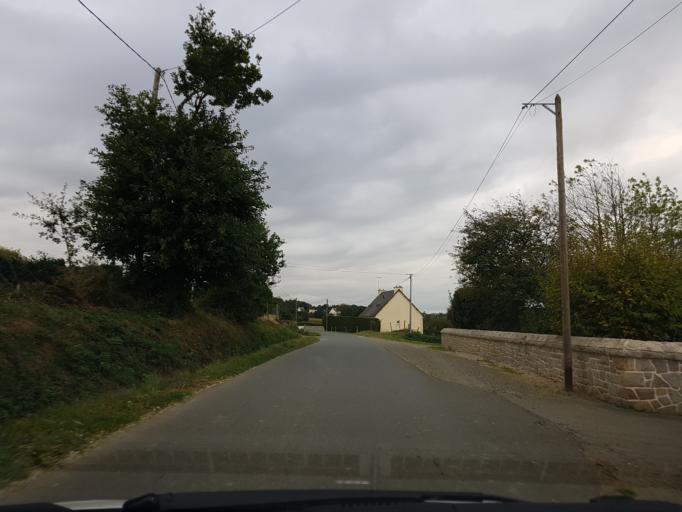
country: FR
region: Brittany
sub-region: Departement des Cotes-d'Armor
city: Pledran
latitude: 48.4678
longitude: -2.7403
